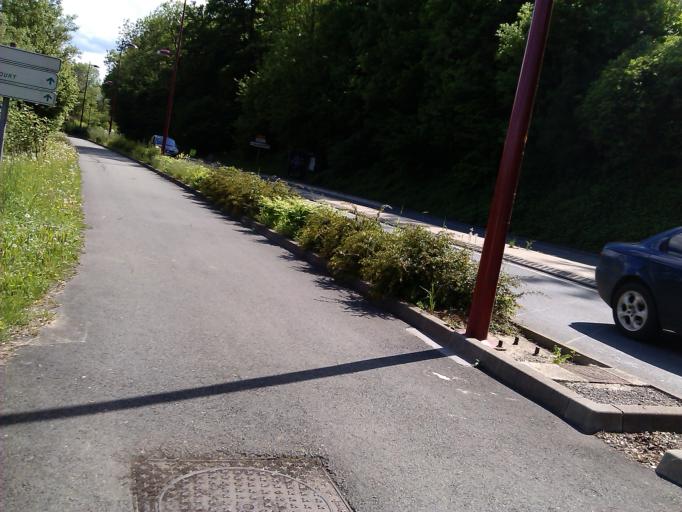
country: FR
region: Franche-Comte
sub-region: Departement du Doubs
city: Sainte-Suzanne
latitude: 47.5002
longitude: 6.7723
